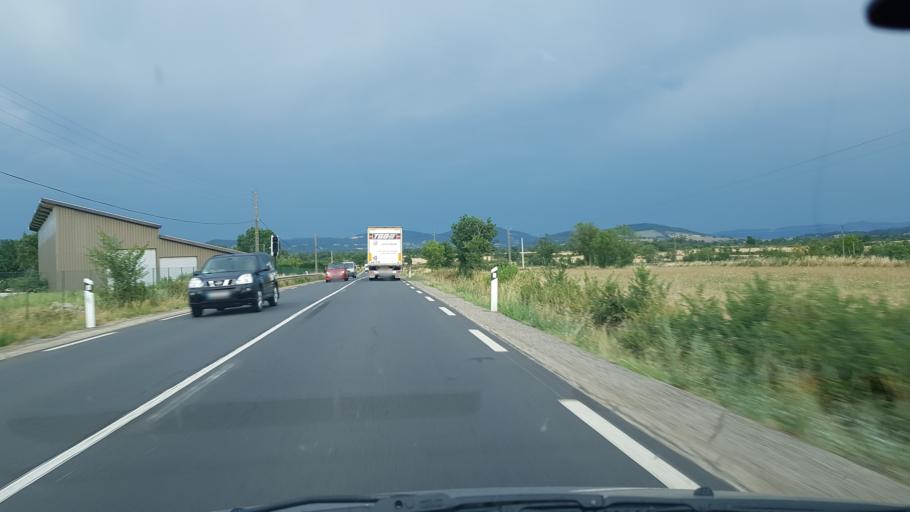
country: FR
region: Auvergne
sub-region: Departement de la Haute-Loire
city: Paulhaguet
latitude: 45.1729
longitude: 3.5239
